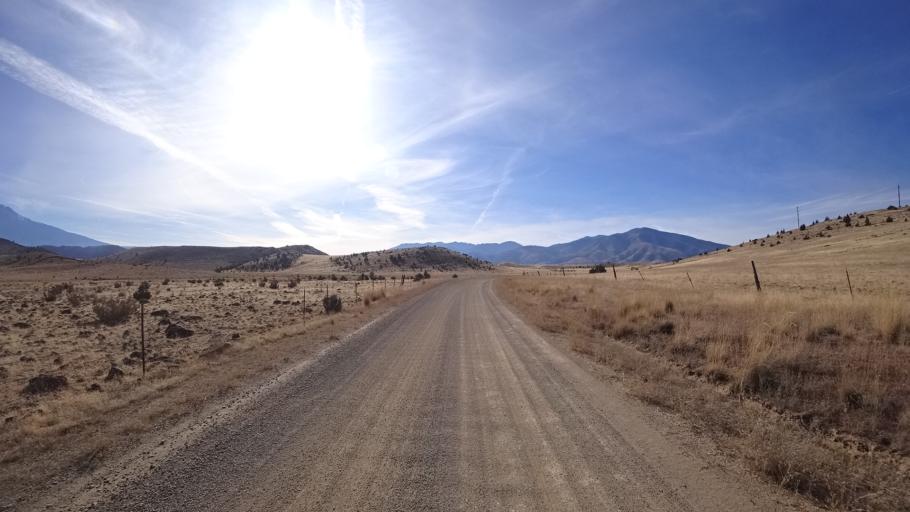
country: US
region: California
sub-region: Siskiyou County
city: Weed
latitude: 41.5341
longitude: -122.4686
